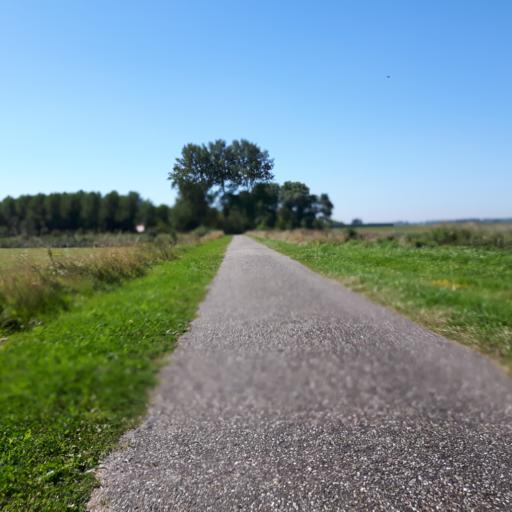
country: NL
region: Zeeland
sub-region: Gemeente Noord-Beveland
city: Kamperland
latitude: 51.5794
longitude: 3.7857
